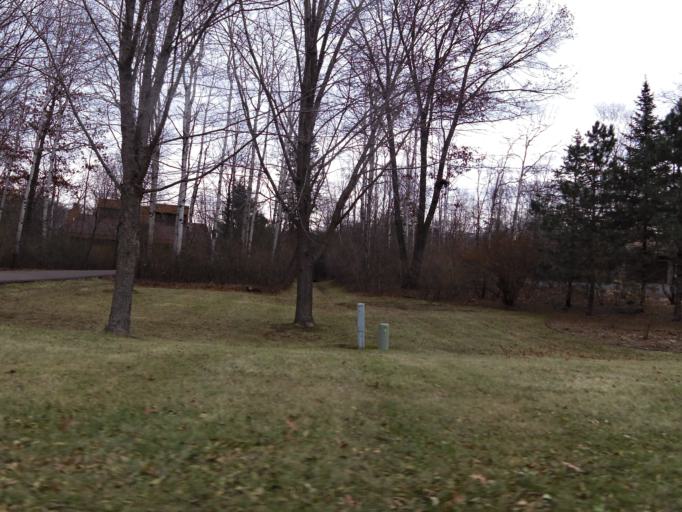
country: US
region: Minnesota
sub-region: Washington County
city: Lake Elmo
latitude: 44.9818
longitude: -92.8729
